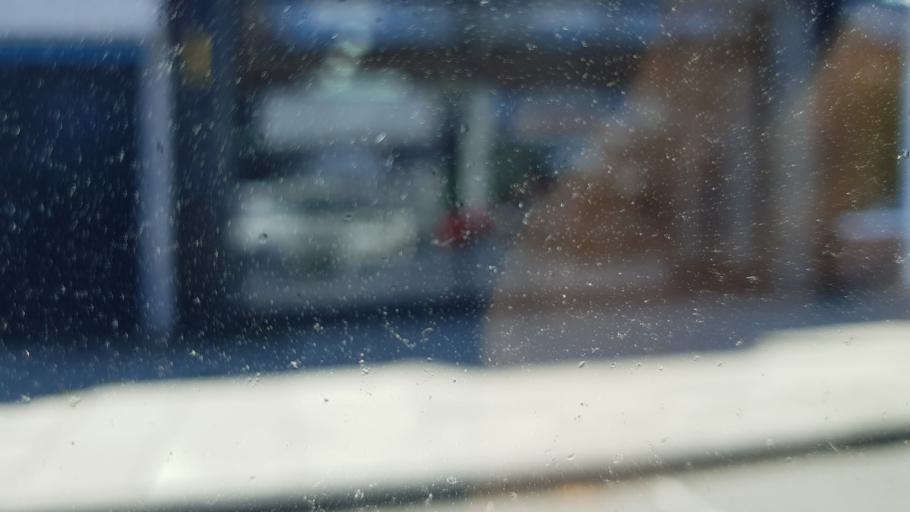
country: GB
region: England
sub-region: Middlesbrough
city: Middlesbrough
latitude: 54.5574
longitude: -1.2477
